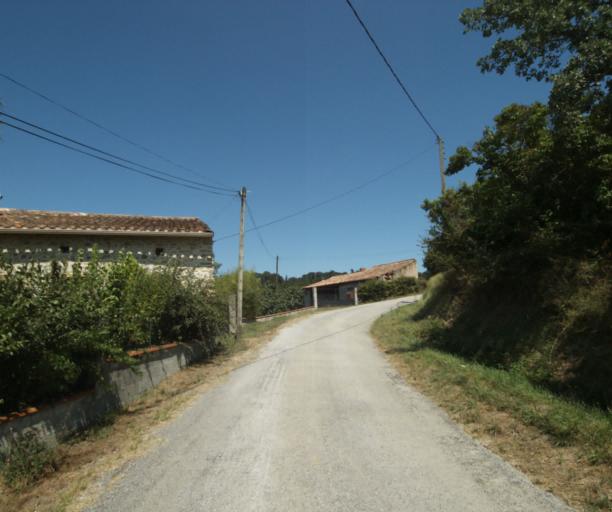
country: FR
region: Midi-Pyrenees
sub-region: Departement de la Haute-Garonne
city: Auriac-sur-Vendinelle
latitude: 43.5032
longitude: 1.8624
